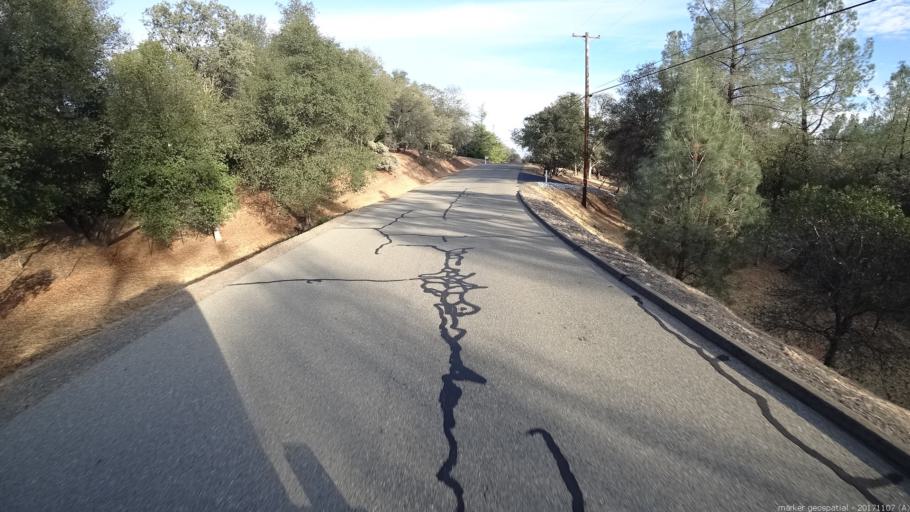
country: US
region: California
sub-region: Shasta County
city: Shasta
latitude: 40.5353
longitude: -122.4834
